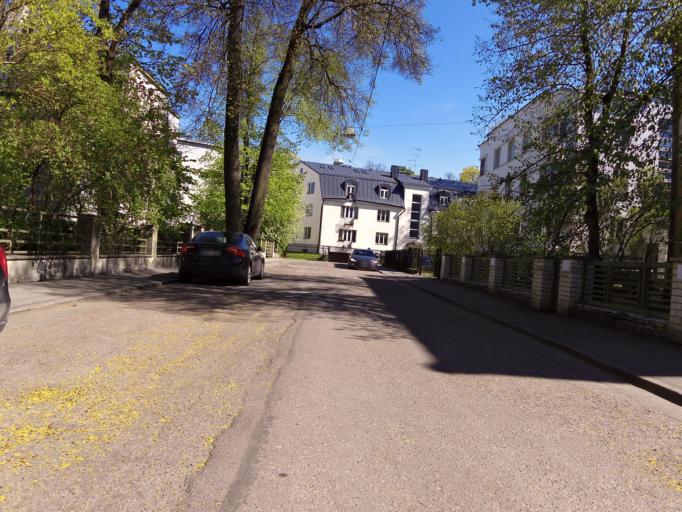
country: EE
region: Harju
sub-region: Tallinna linn
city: Tallinn
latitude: 59.4366
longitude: 24.7812
